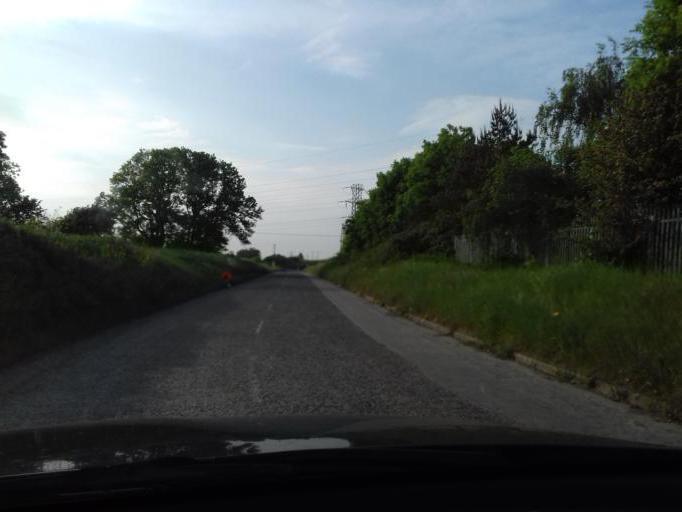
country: IE
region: Leinster
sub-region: Dublin City
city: Finglas
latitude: 53.4039
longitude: -6.3156
